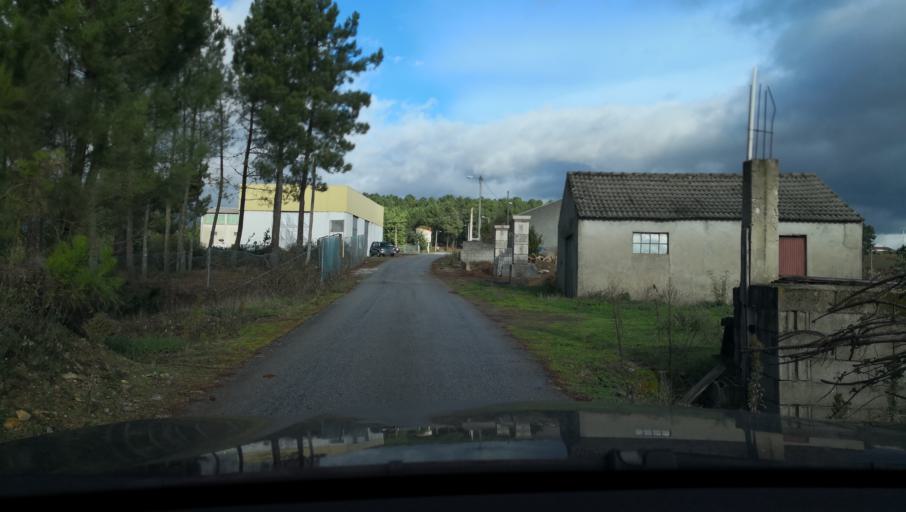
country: PT
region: Vila Real
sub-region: Vila Real
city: Vila Real
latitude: 41.2703
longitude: -7.7156
